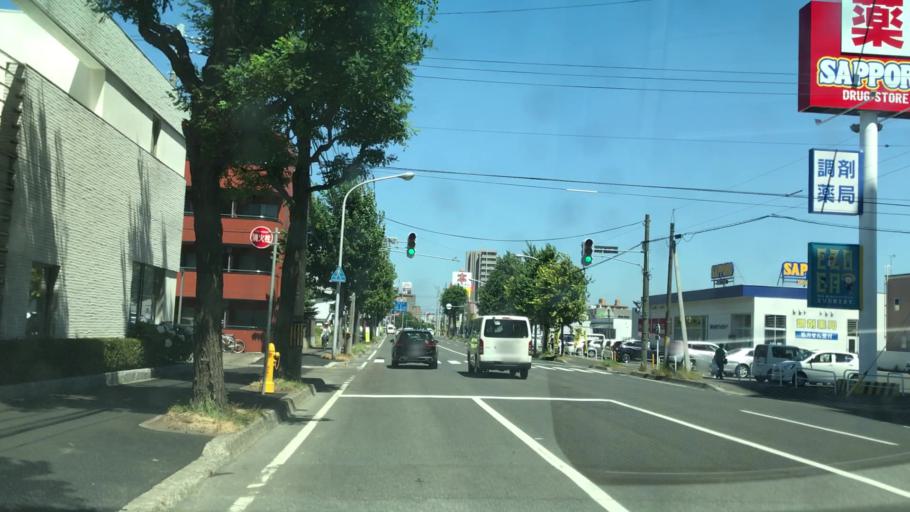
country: JP
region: Hokkaido
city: Sapporo
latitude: 43.0663
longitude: 141.3064
